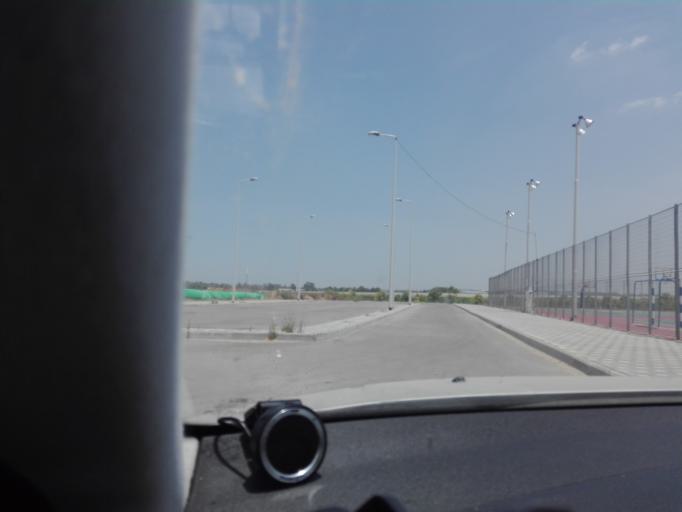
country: IL
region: Central District
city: Bene 'Ayish
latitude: 31.7421
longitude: 34.7427
